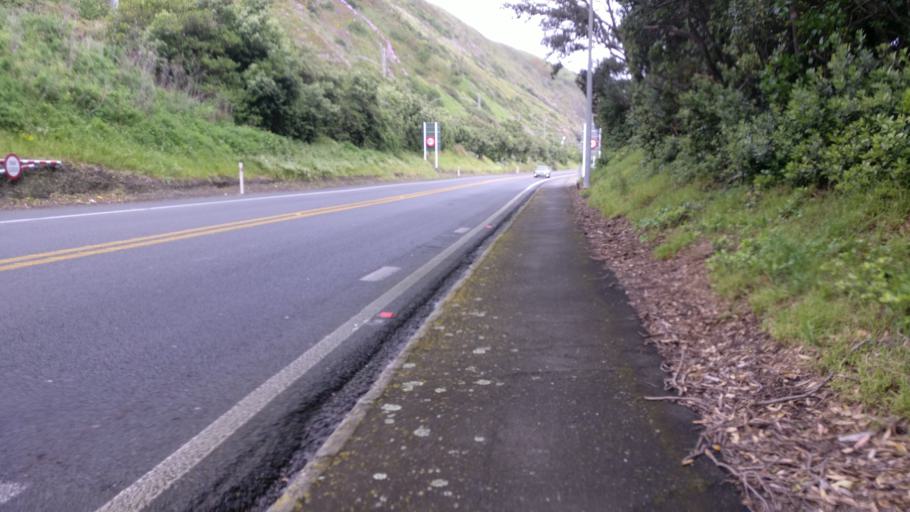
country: NZ
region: Wellington
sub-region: Kapiti Coast District
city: Paraparaumu
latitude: -40.9994
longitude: 174.9403
